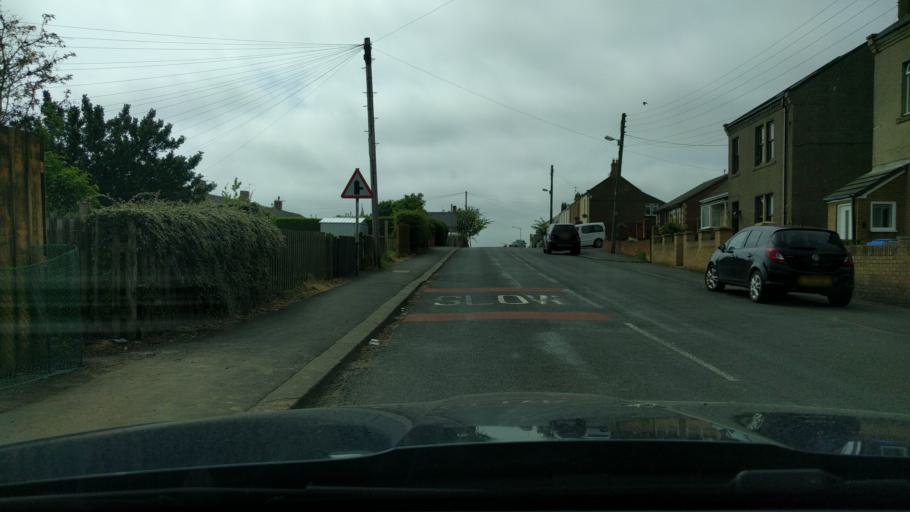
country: GB
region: England
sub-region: Northumberland
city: Acklington
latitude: 55.3057
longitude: -1.6147
